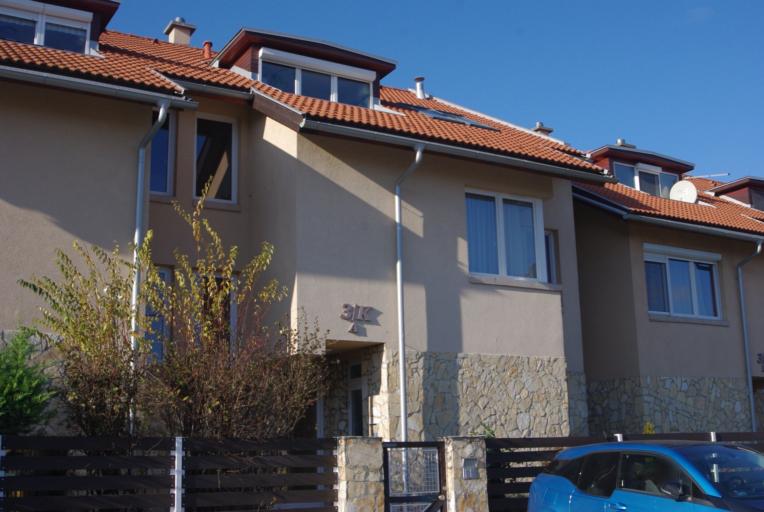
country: HU
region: Pest
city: Urom
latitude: 47.5885
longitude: 19.0299
